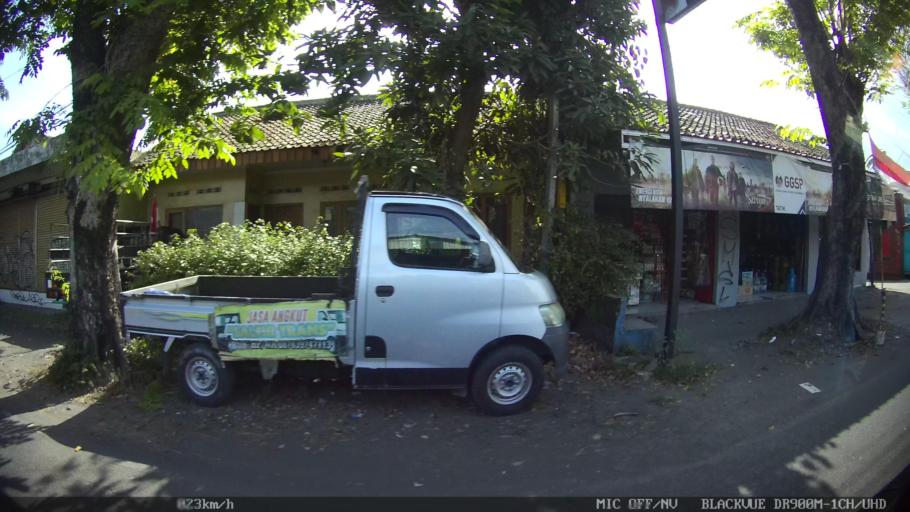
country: ID
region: Daerah Istimewa Yogyakarta
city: Kasihan
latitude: -7.8318
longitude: 110.3536
